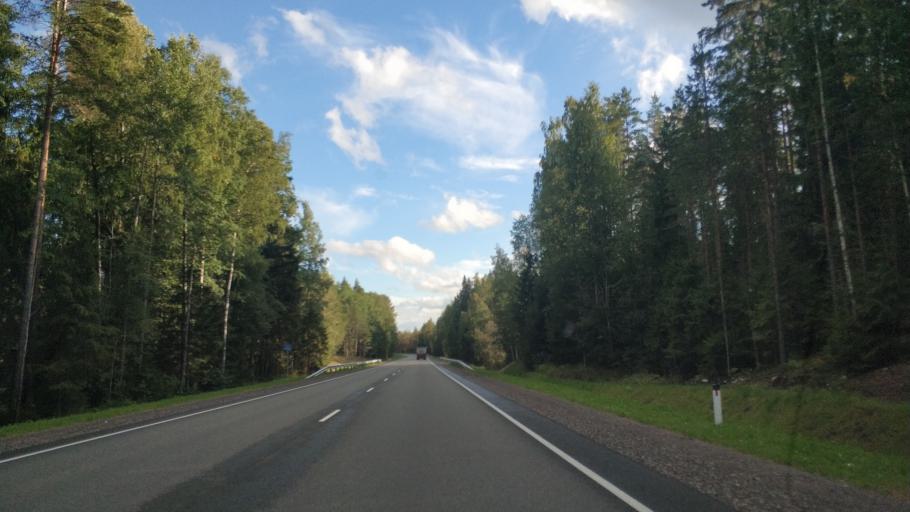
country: RU
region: Leningrad
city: Priozersk
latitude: 60.8960
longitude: 30.1596
